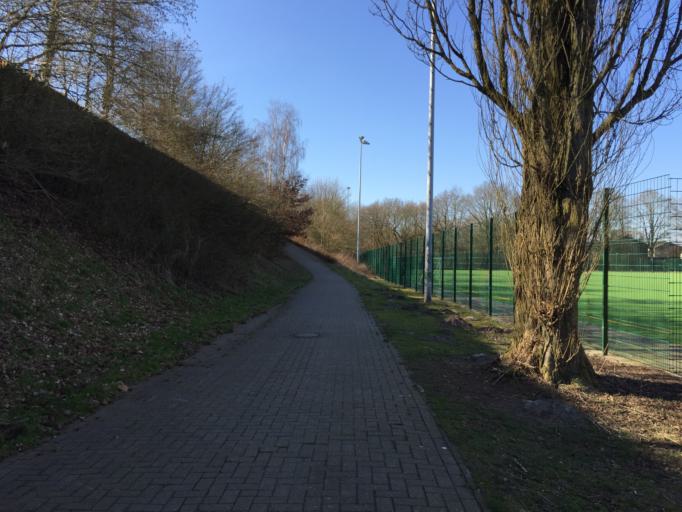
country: DE
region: Lower Saxony
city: Oldenburg
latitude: 53.1626
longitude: 8.2317
